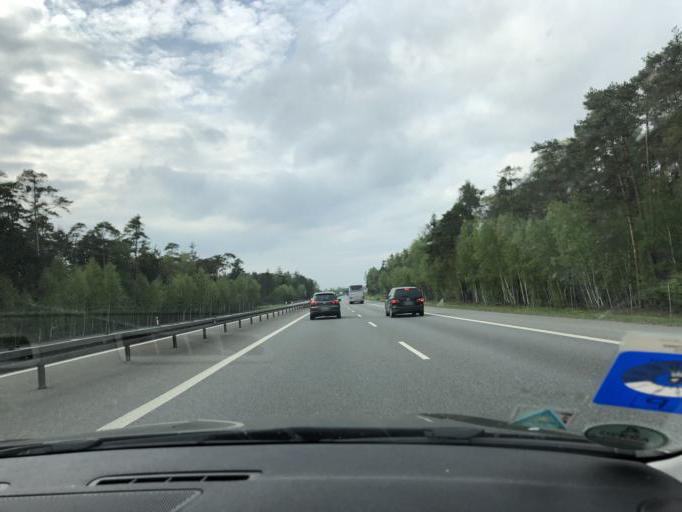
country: PL
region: Opole Voivodeship
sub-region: Powiat opolski
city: Dabrowa
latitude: 50.6341
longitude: 17.7417
